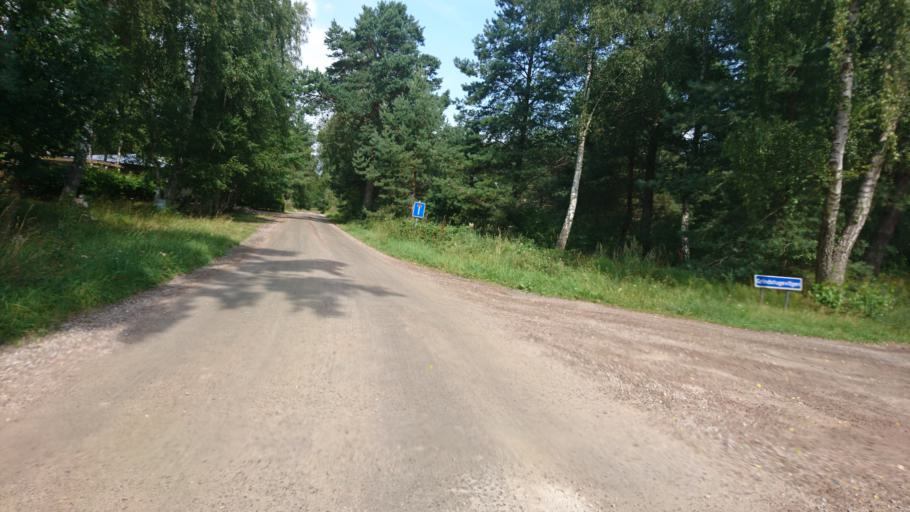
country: SE
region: Skane
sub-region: Vellinge Kommun
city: Ljunghusen
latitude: 55.4027
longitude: 12.9099
